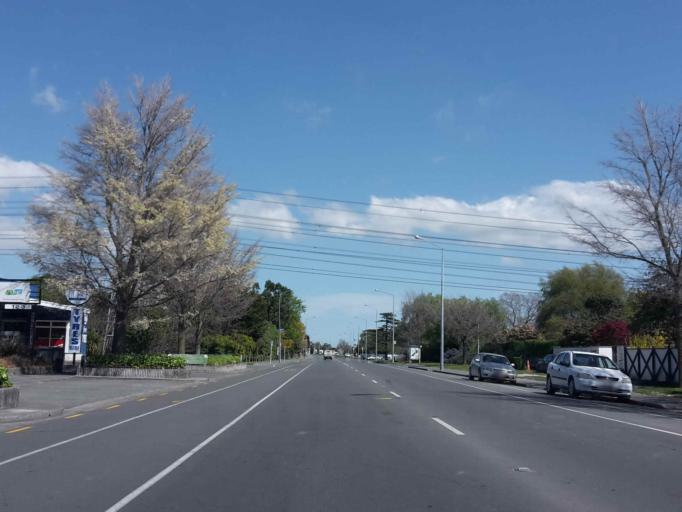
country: NZ
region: Canterbury
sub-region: Selwyn District
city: Prebbleton
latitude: -43.5371
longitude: 172.5580
